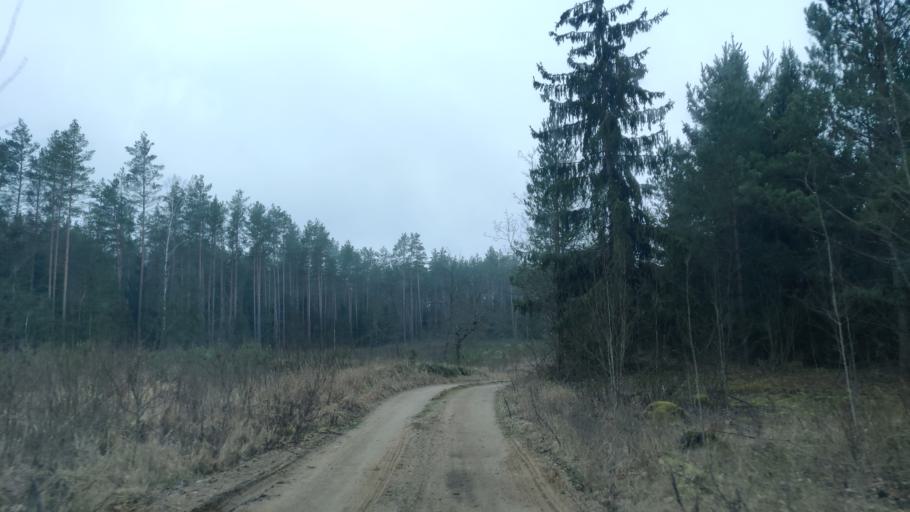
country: LT
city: Trakai
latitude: 54.5582
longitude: 24.9563
